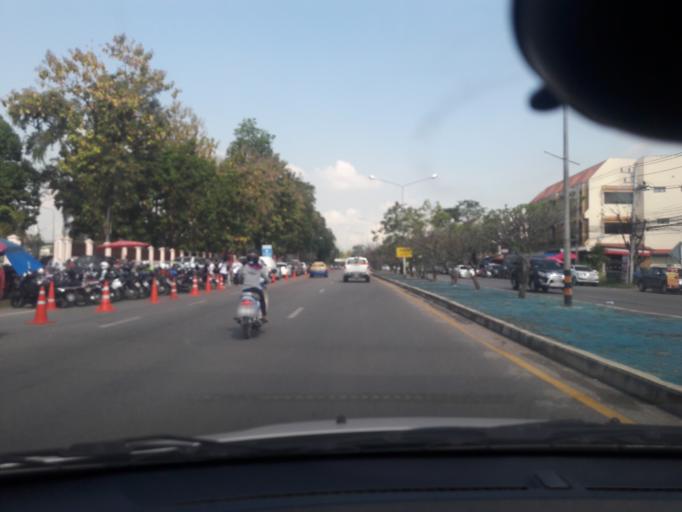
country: TH
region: Lampang
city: Lampang
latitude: 18.2322
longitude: 99.4904
